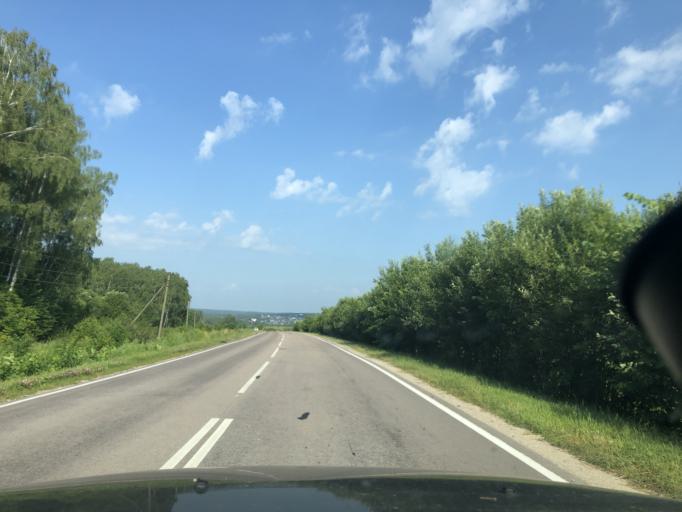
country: RU
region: Tula
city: Dubna
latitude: 54.1405
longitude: 37.0110
